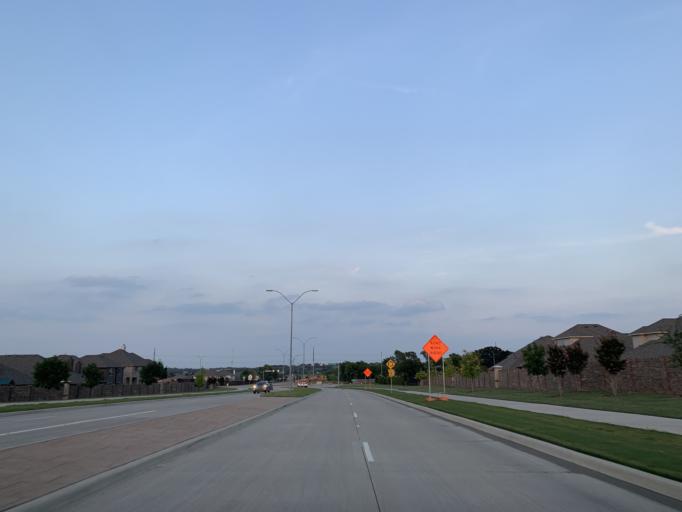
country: US
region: Texas
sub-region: Tarrant County
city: Keller
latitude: 32.9553
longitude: -97.2670
